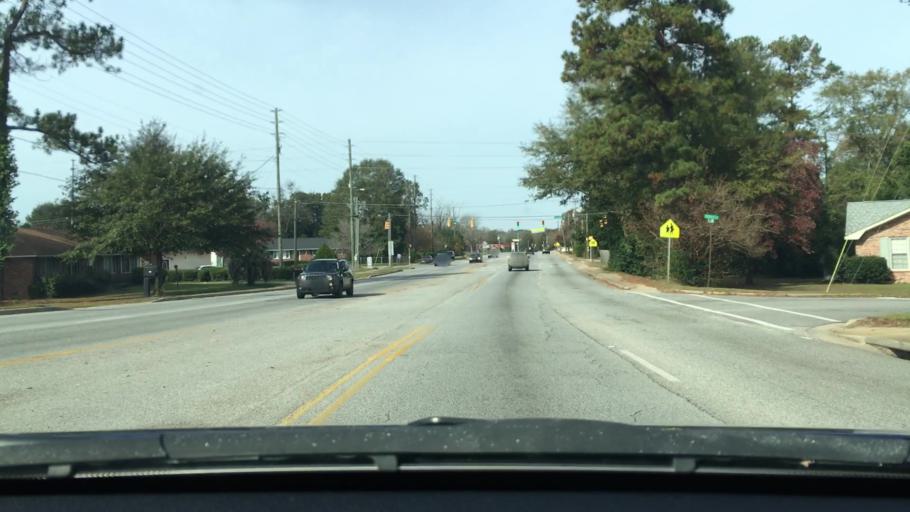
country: US
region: South Carolina
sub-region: Sumter County
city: South Sumter
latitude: 33.9103
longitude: -80.3820
